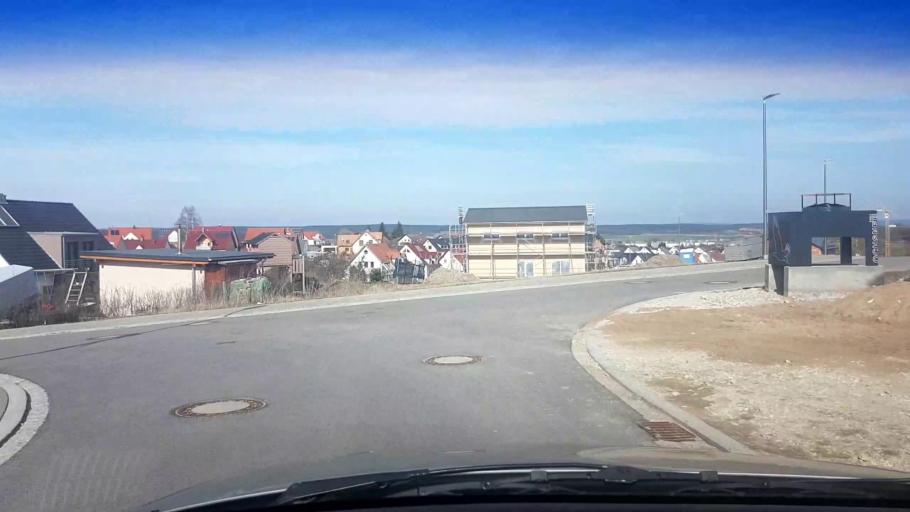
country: DE
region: Bavaria
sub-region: Upper Franconia
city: Burgebrach
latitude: 49.8194
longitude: 10.7393
